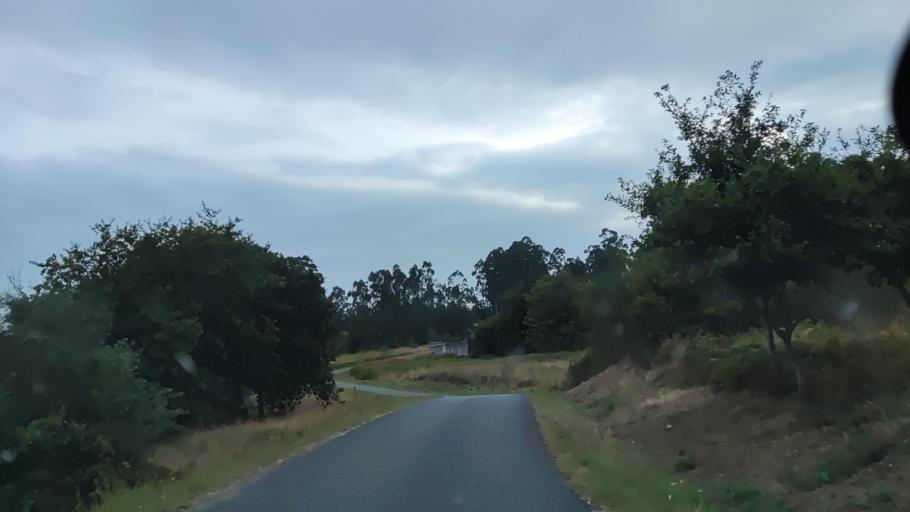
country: ES
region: Galicia
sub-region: Provincia da Coruna
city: Padron
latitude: 42.7233
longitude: -8.6773
